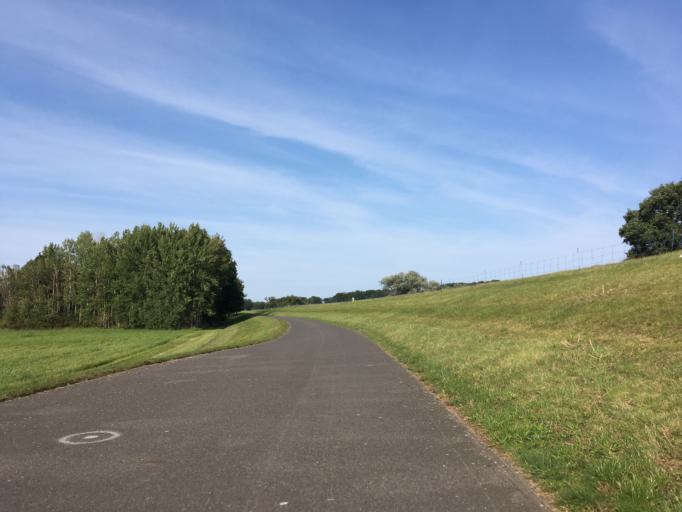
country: DE
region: Brandenburg
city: Vogelsang
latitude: 52.2175
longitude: 14.7057
